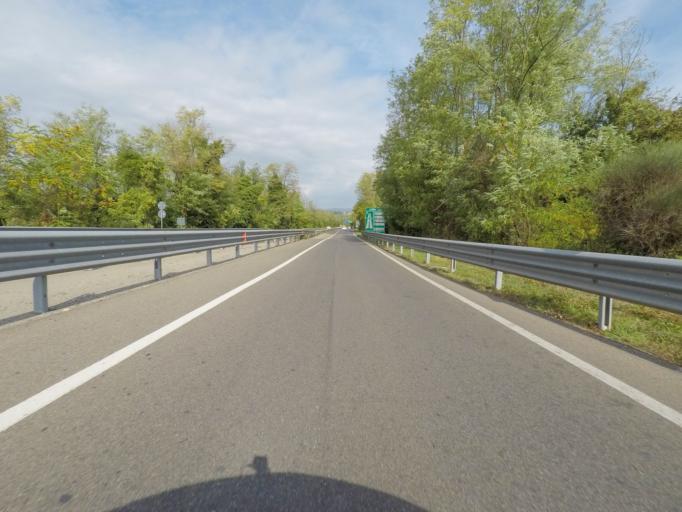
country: IT
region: Tuscany
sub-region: Provincia di Siena
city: Belverde
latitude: 43.3506
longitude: 11.3060
